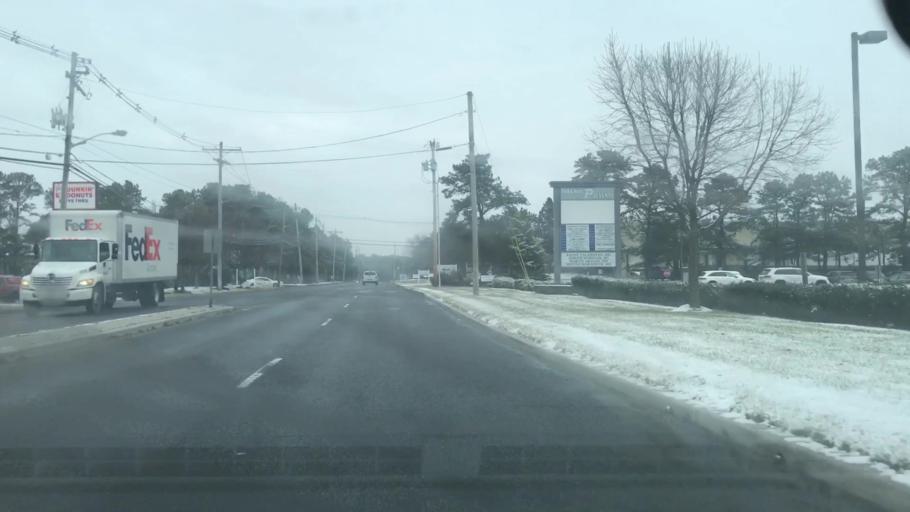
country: US
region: New Jersey
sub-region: Ocean County
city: Leisure Village
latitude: 40.0540
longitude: -74.1791
